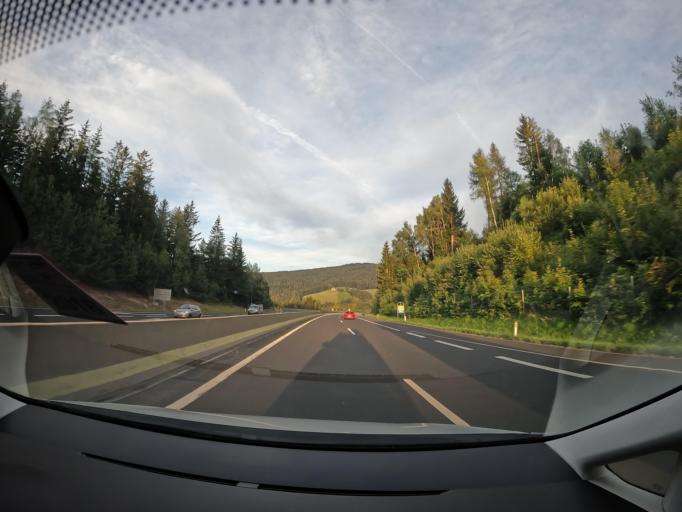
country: AT
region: Styria
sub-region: Politischer Bezirk Voitsberg
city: Voitsberg
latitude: 46.9903
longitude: 15.1186
